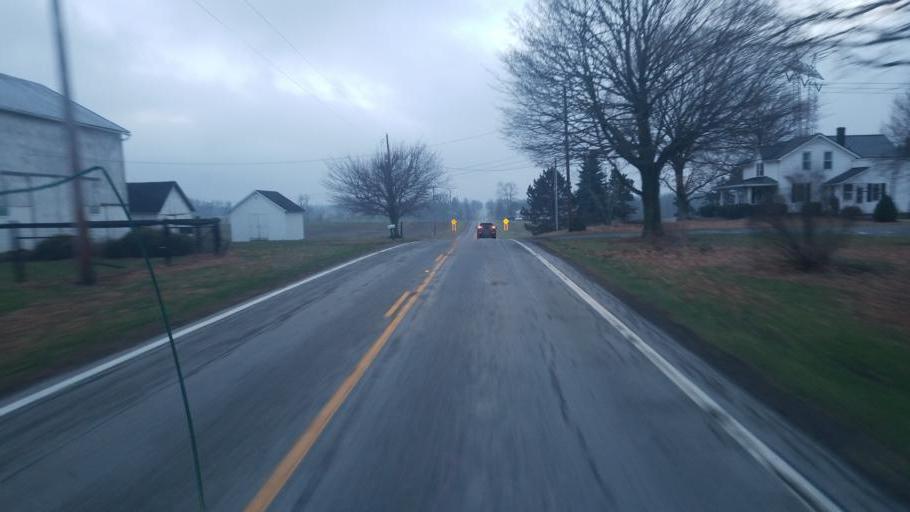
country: US
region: Ohio
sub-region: Wyandot County
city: Upper Sandusky
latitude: 40.8950
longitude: -83.1317
